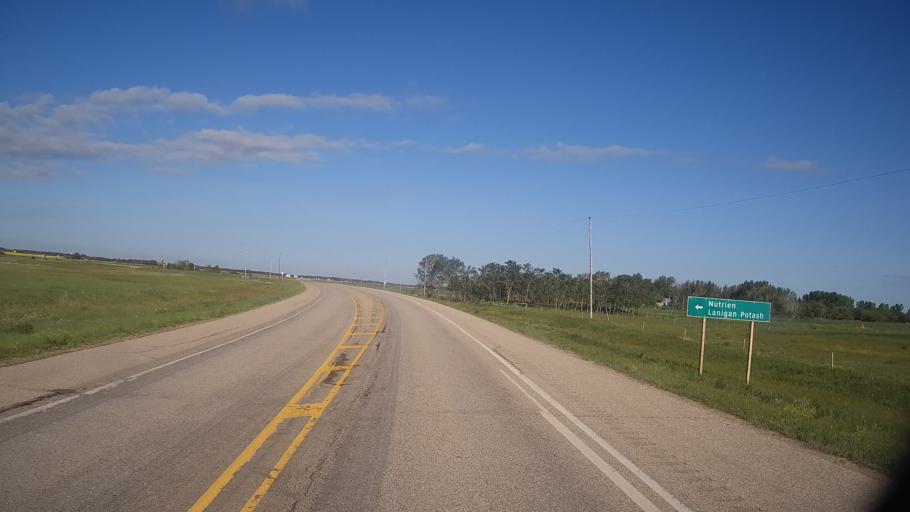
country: CA
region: Saskatchewan
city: Lanigan
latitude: 51.8754
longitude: -105.1871
